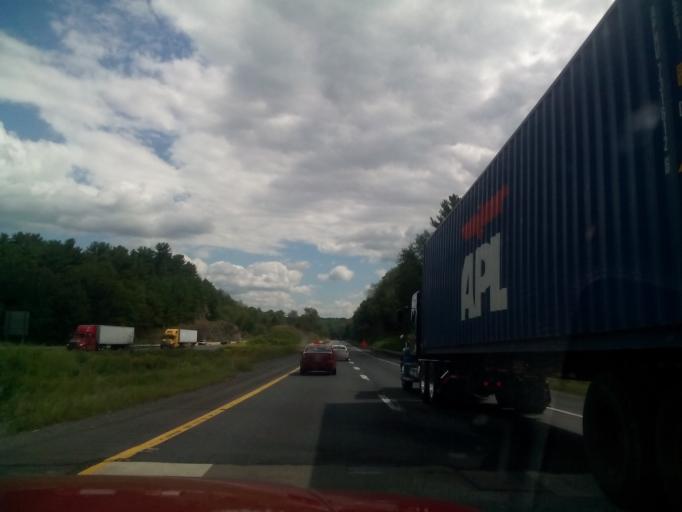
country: US
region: Pennsylvania
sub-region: Monroe County
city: Tannersville
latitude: 41.0226
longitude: -75.3052
